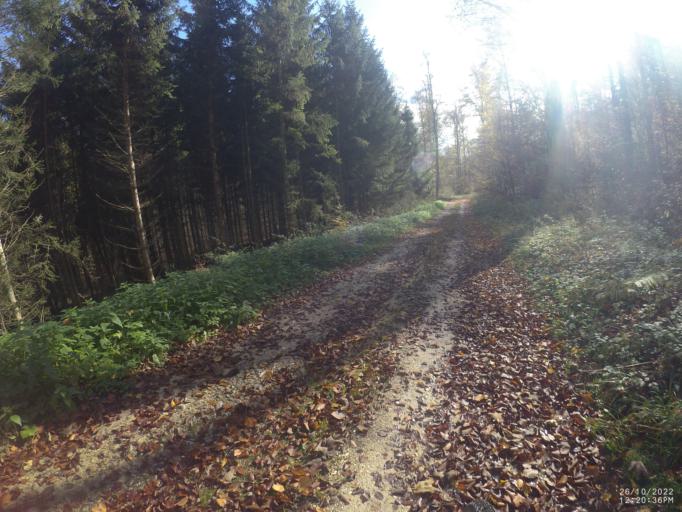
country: DE
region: Baden-Wuerttemberg
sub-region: Regierungsbezirk Stuttgart
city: Wiesensteig
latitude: 48.5421
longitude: 9.6117
